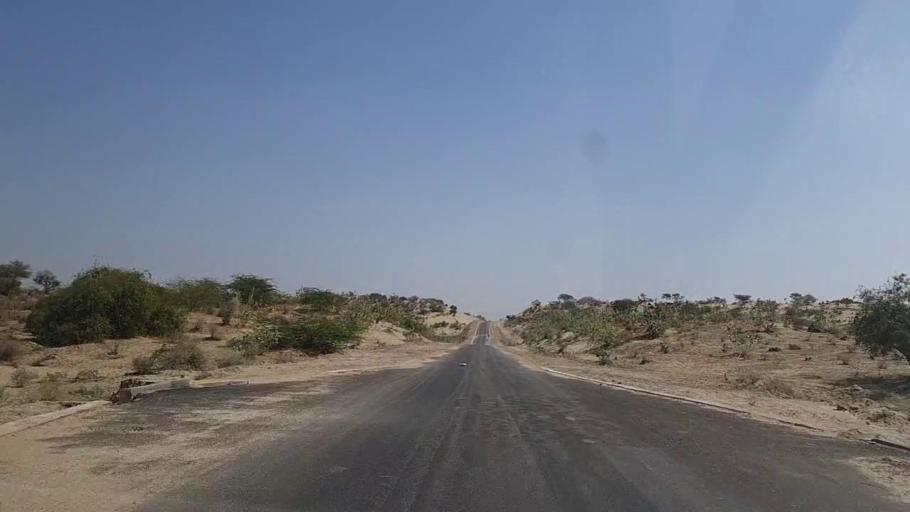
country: PK
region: Sindh
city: Diplo
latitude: 24.4829
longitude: 69.4759
